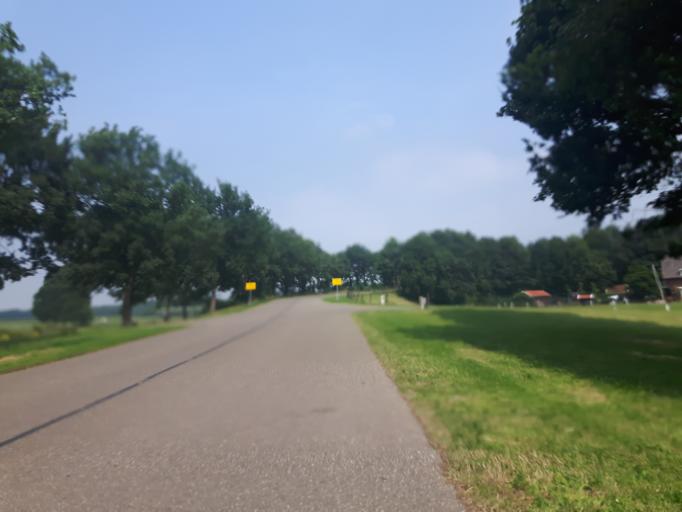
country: NL
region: Overijssel
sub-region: Gemeente Borne
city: Borne
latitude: 52.3024
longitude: 6.7119
